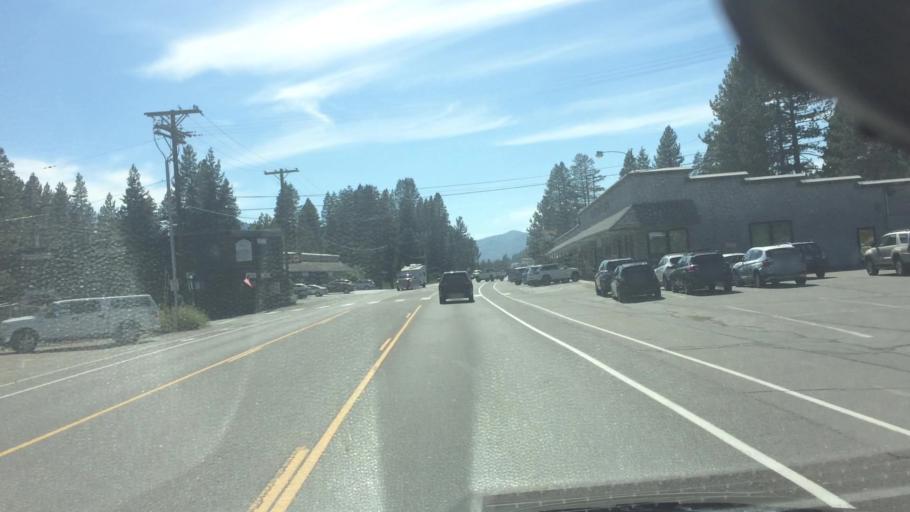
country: US
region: California
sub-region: Nevada County
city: Truckee
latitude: 39.3263
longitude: -120.2020
